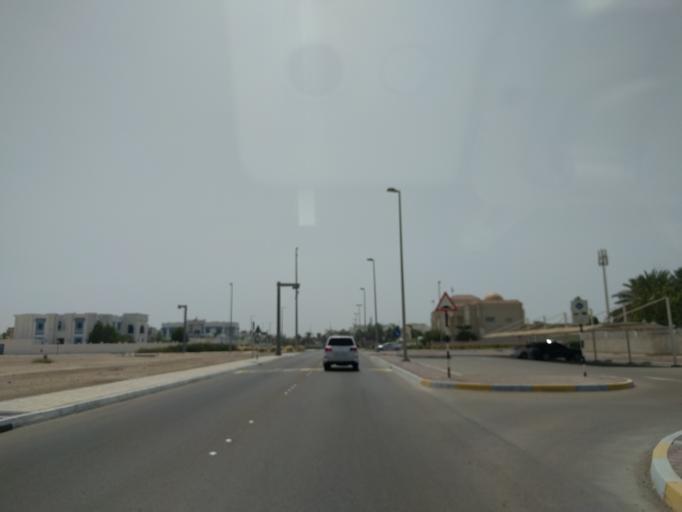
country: AE
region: Abu Dhabi
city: Abu Dhabi
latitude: 24.4255
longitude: 54.4311
